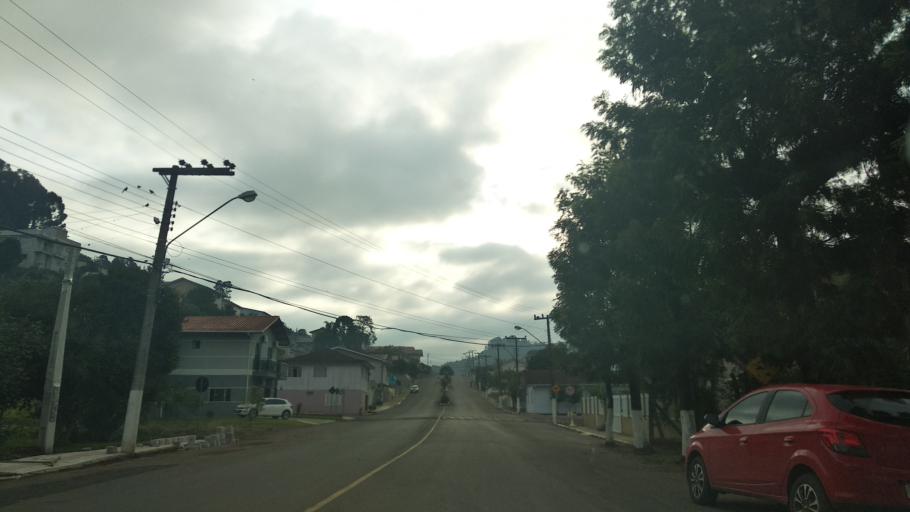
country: BR
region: Santa Catarina
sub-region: Videira
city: Videira
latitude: -27.0464
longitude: -51.2328
